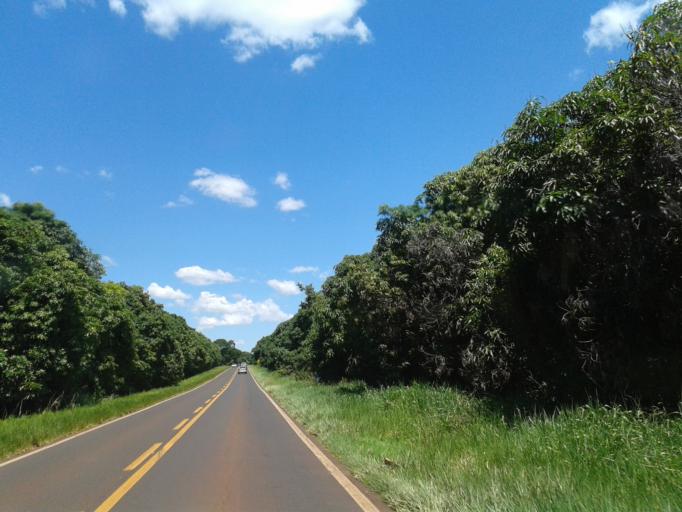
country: BR
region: Minas Gerais
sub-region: Centralina
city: Centralina
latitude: -18.7220
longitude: -49.1603
